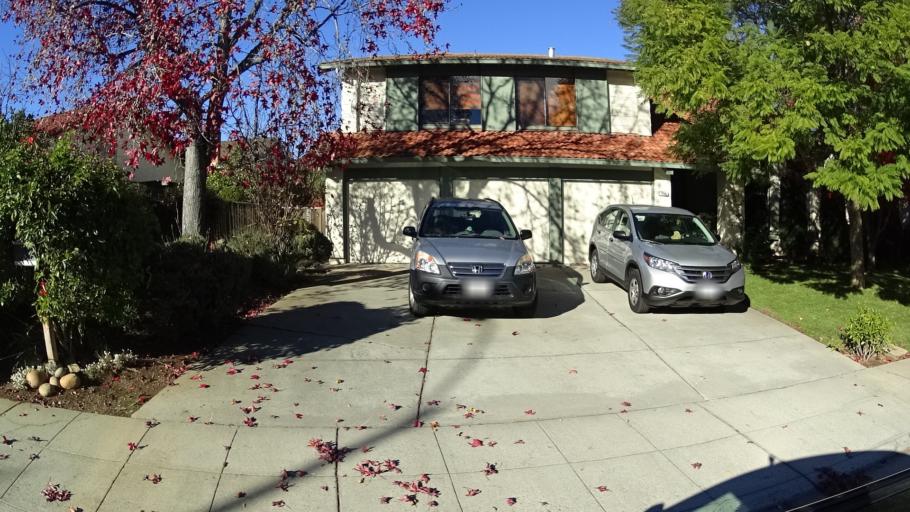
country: US
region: California
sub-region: Santa Clara County
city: Cupertino
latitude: 37.3389
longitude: -122.0253
